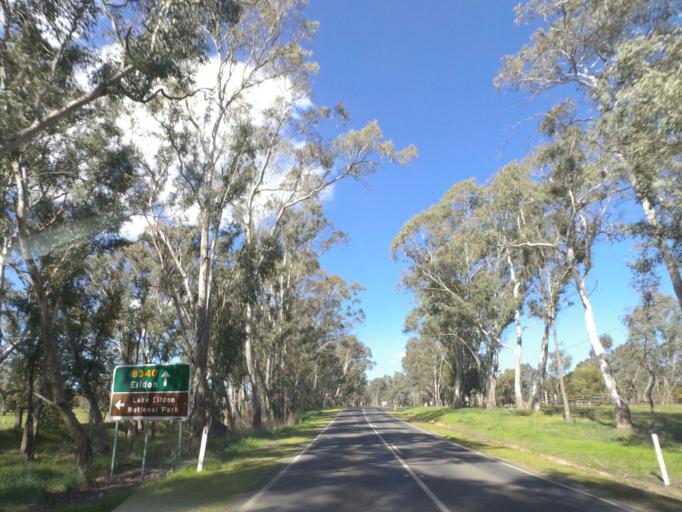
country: AU
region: Victoria
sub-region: Murrindindi
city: Alexandra
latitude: -37.1932
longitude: 145.7288
